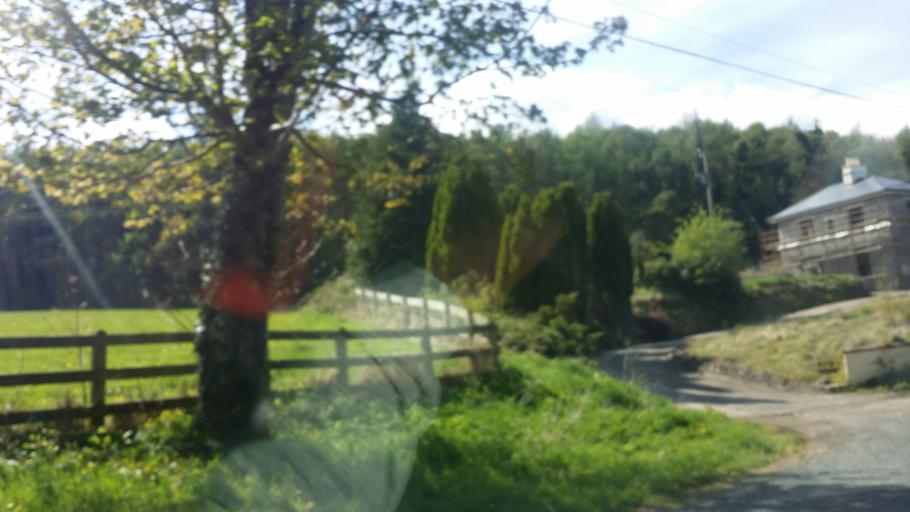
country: GB
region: Northern Ireland
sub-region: Fermanagh District
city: Enniskillen
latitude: 54.4110
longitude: -7.7244
